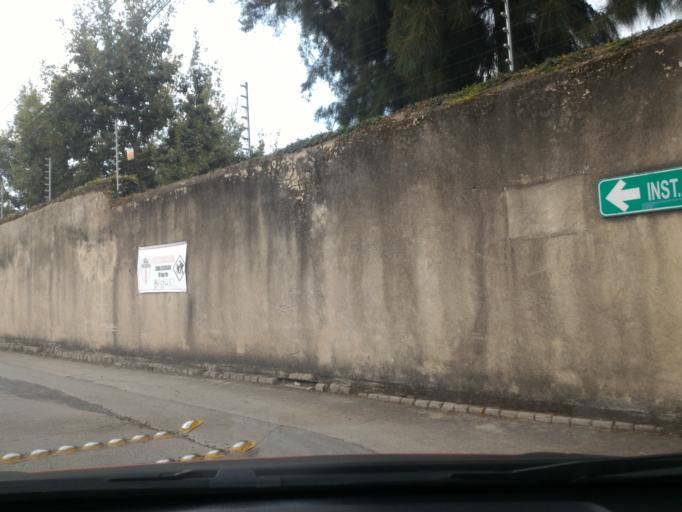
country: MX
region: Jalisco
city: Nuevo Mexico
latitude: 20.7009
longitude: -103.4703
